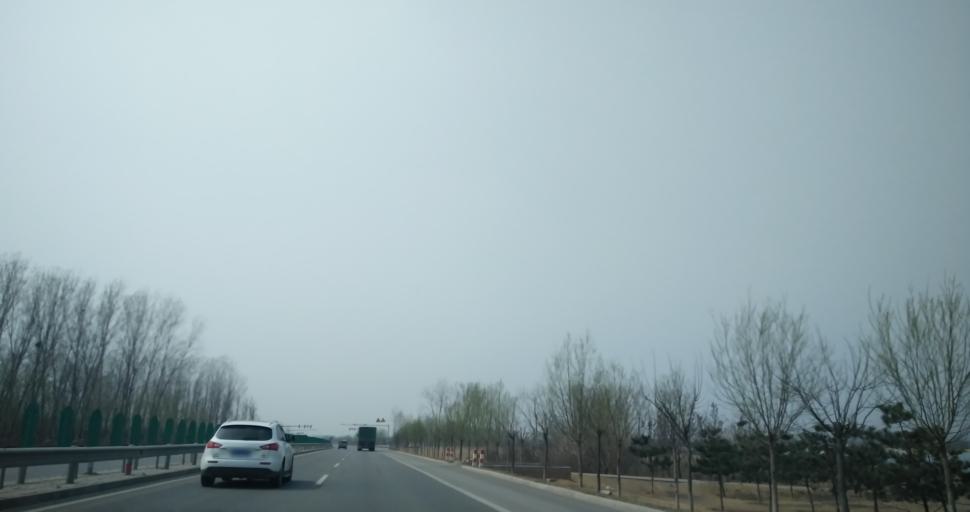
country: CN
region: Beijing
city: Weishanzhuang
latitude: 39.6793
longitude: 116.4360
